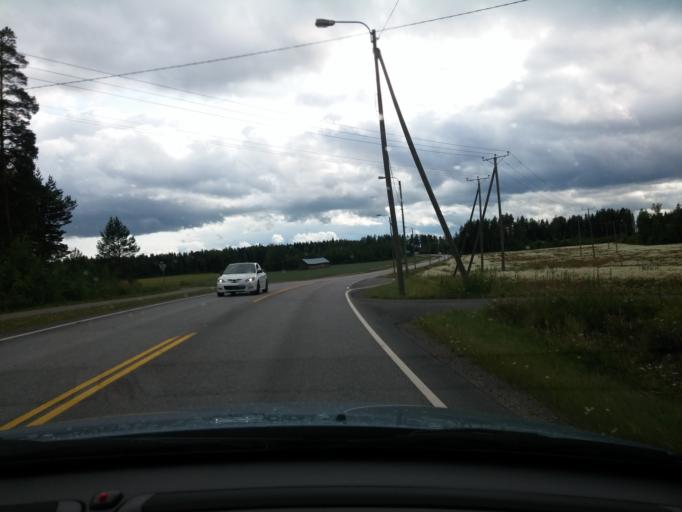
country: FI
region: Uusimaa
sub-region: Porvoo
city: Askola
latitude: 60.5086
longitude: 25.5725
